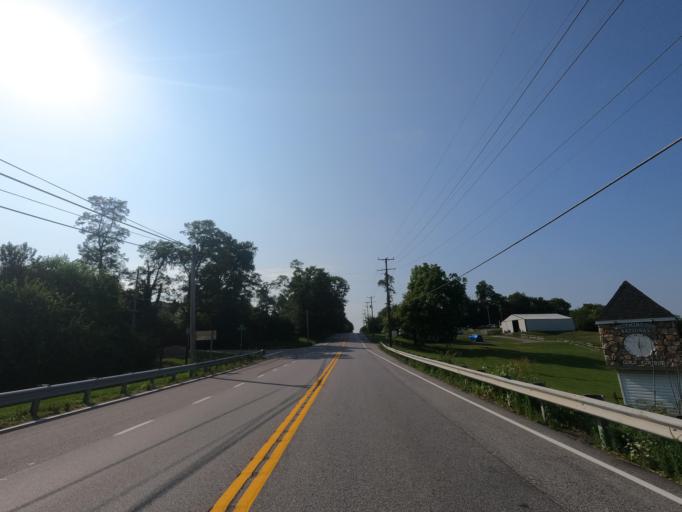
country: US
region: Maryland
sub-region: Carroll County
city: Westminster
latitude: 39.6357
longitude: -77.0048
